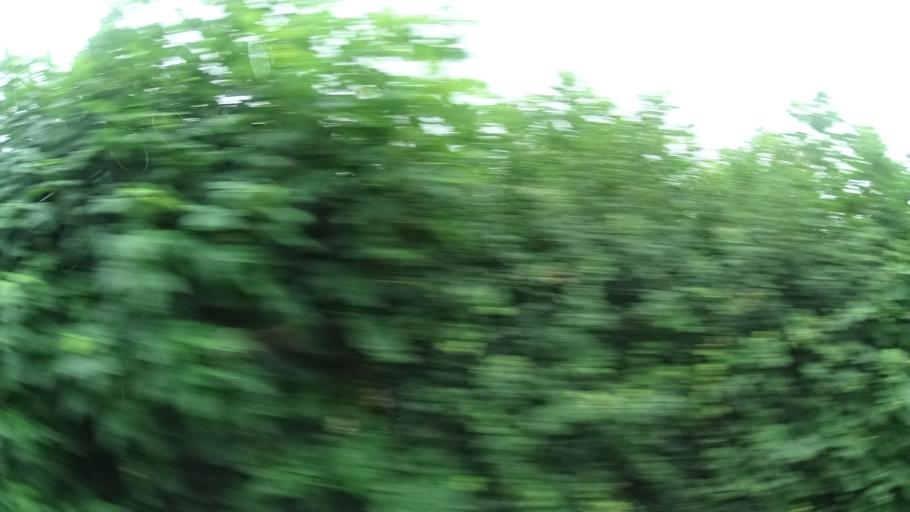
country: LU
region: Grevenmacher
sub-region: Canton de Remich
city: Dalheim
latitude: 49.5311
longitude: 6.2521
